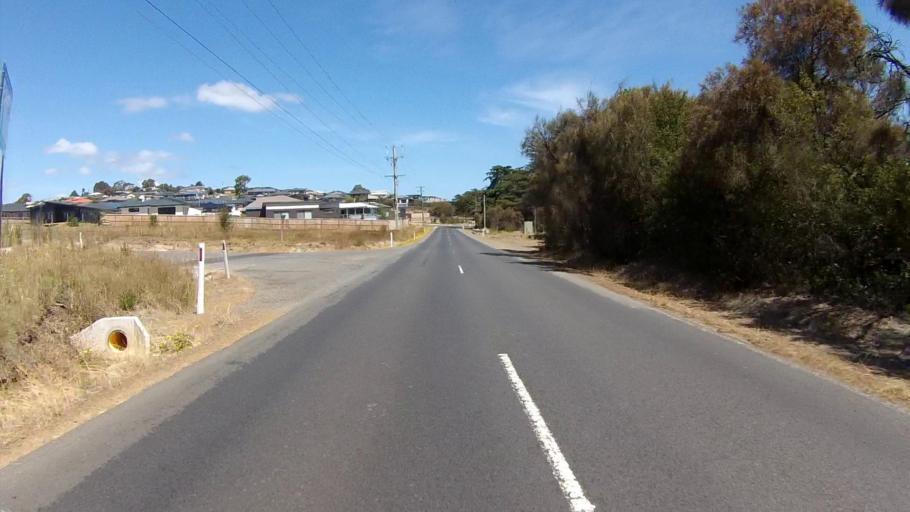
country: AU
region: Tasmania
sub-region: Sorell
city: Sorell
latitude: -42.7913
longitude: 147.5243
